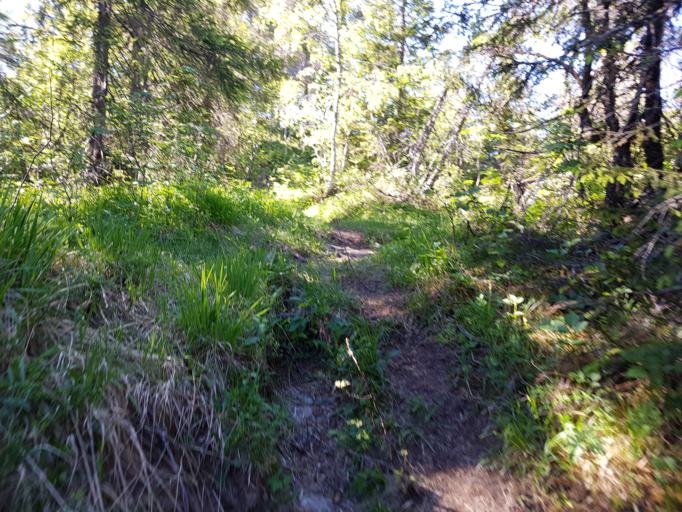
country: NO
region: Sor-Trondelag
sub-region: Trondheim
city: Trondheim
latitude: 63.4095
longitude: 10.3117
